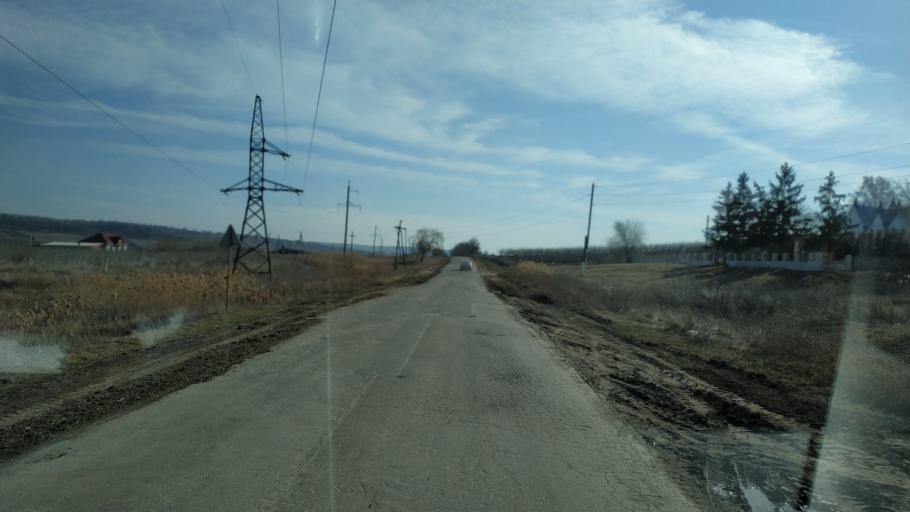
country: MD
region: Nisporeni
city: Nisporeni
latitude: 47.0873
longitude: 28.1393
